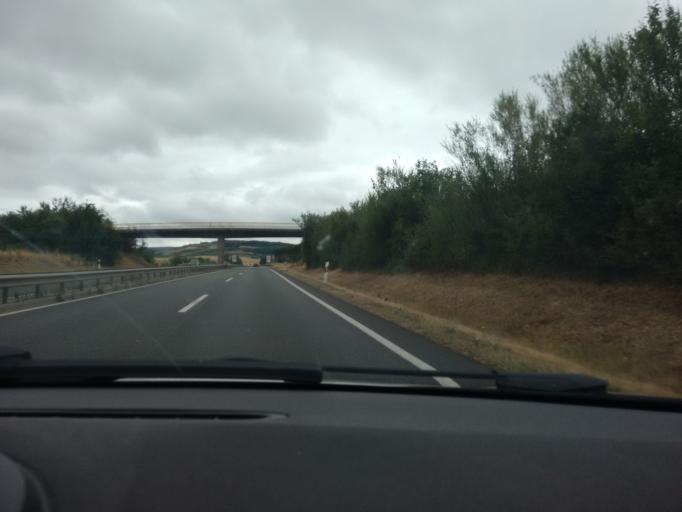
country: DE
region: Rheinland-Pfalz
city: Weinsheim
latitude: 49.8257
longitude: 7.7602
